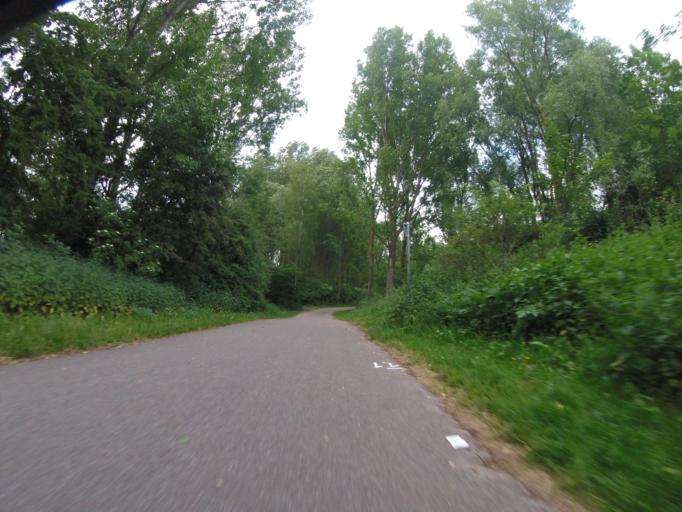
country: NL
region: North Holland
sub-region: Gemeente Haarlemmermeer
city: Hoofddorp
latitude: 52.3254
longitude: 4.6631
